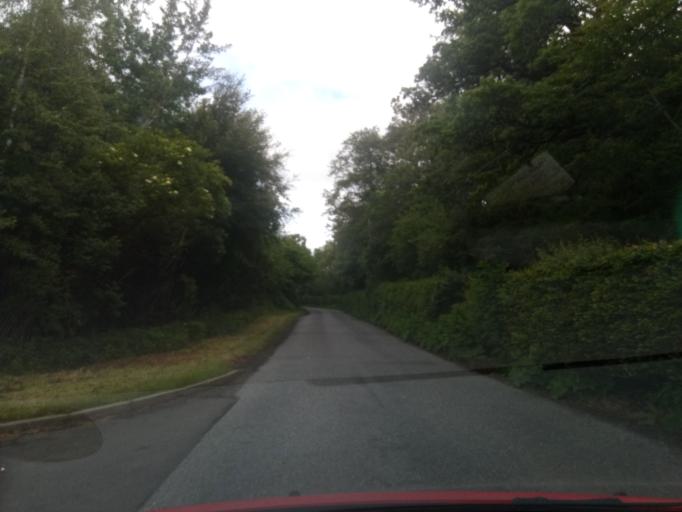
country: GB
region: Scotland
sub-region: The Scottish Borders
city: Selkirk
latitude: 55.5375
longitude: -2.8626
